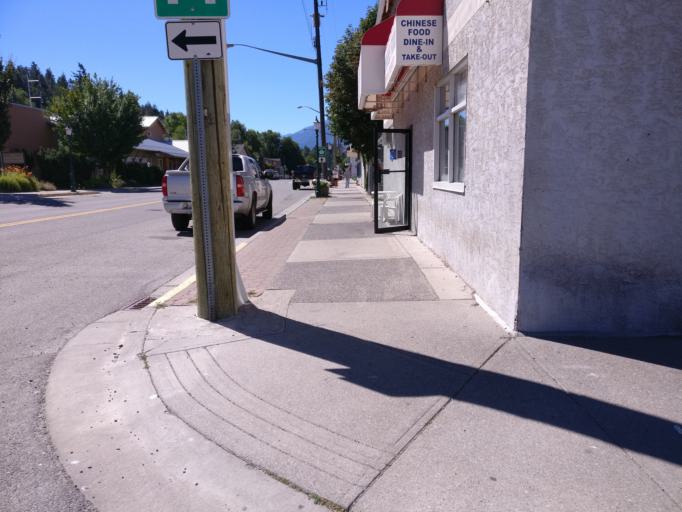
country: CA
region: British Columbia
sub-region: Thompson-Nicola Regional District
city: Ashcroft
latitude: 50.2327
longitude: -121.5810
